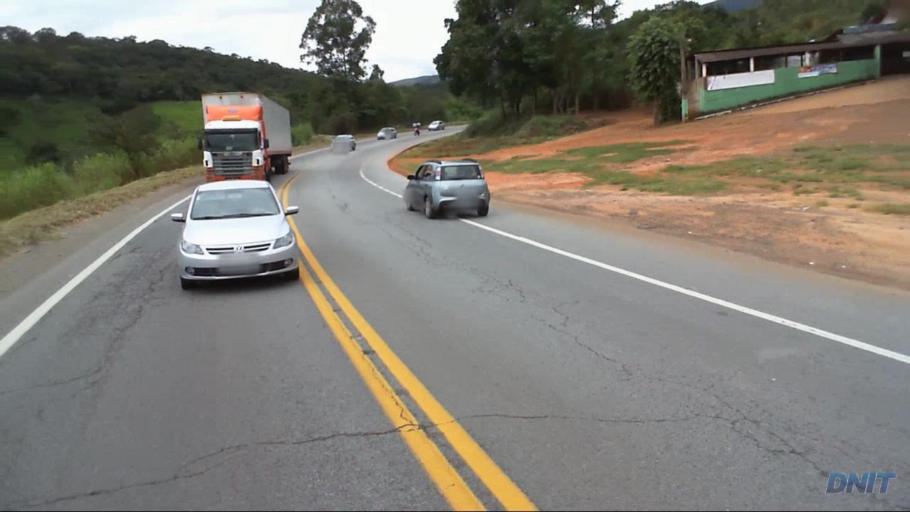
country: BR
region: Minas Gerais
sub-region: Joao Monlevade
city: Joao Monlevade
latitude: -19.8488
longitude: -43.2538
